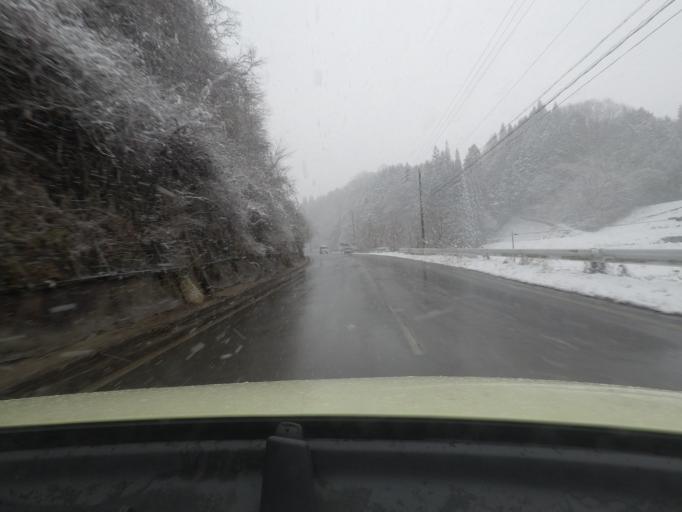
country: JP
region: Gifu
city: Takayama
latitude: 36.1377
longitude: 137.3438
